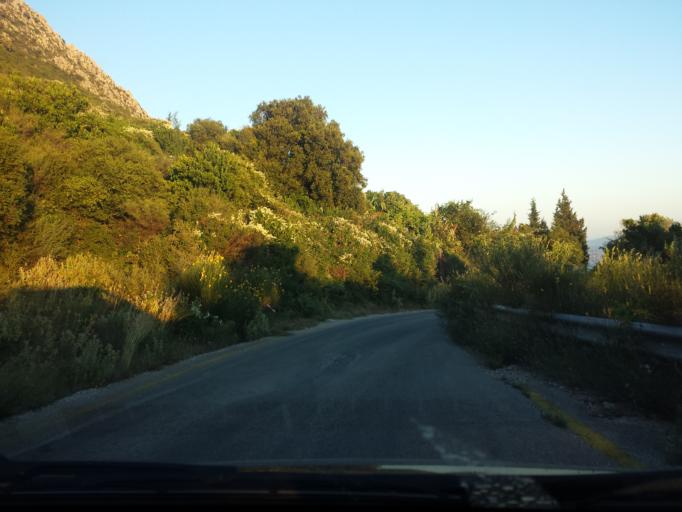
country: GR
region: Ionian Islands
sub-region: Nomos Kerkyras
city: Acharavi
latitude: 39.7288
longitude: 19.8331
